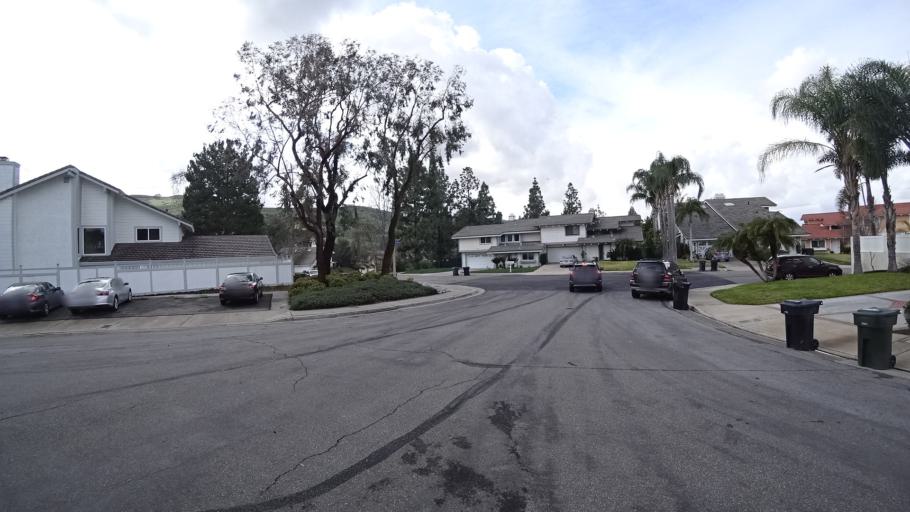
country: US
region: California
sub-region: Orange County
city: Villa Park
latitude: 33.8418
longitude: -117.7798
